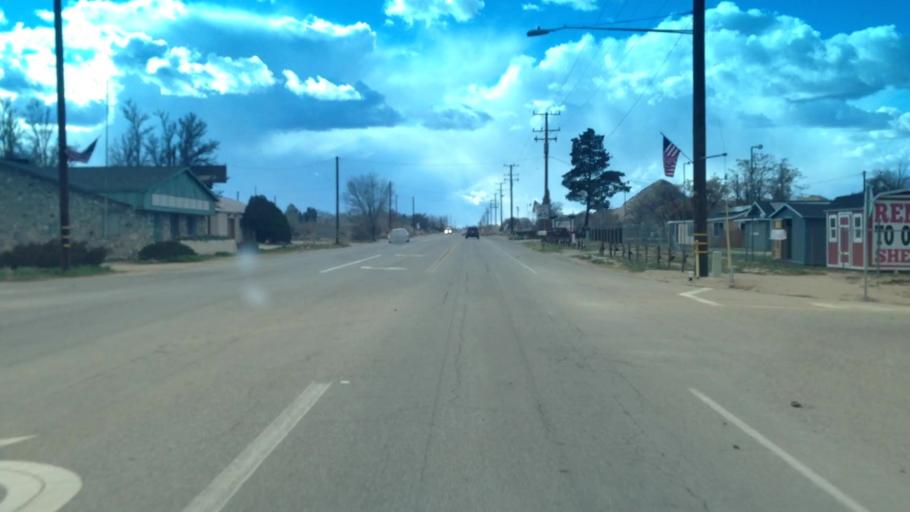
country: US
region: California
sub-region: San Bernardino County
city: Lucerne Valley
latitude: 34.4438
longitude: -116.9631
